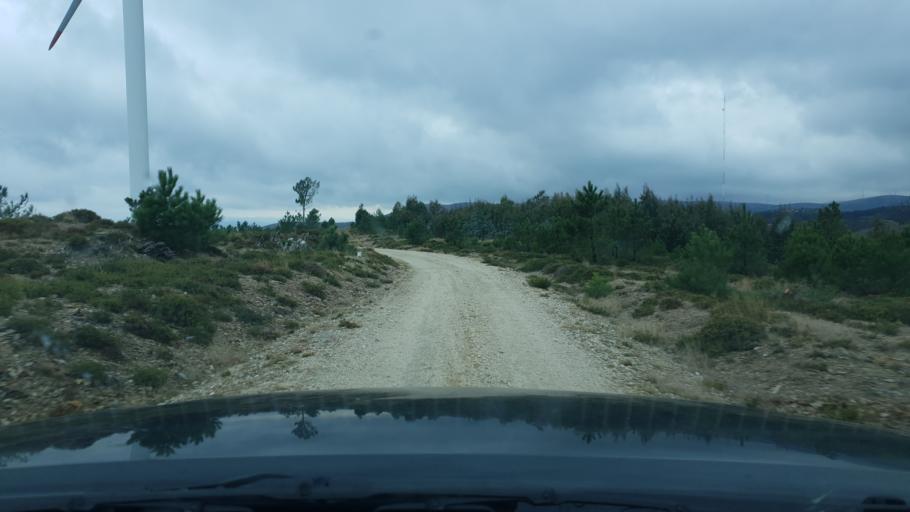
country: PT
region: Viseu
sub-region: Sao Pedro do Sul
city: Sao Pedro do Sul
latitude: 40.8662
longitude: -8.0819
